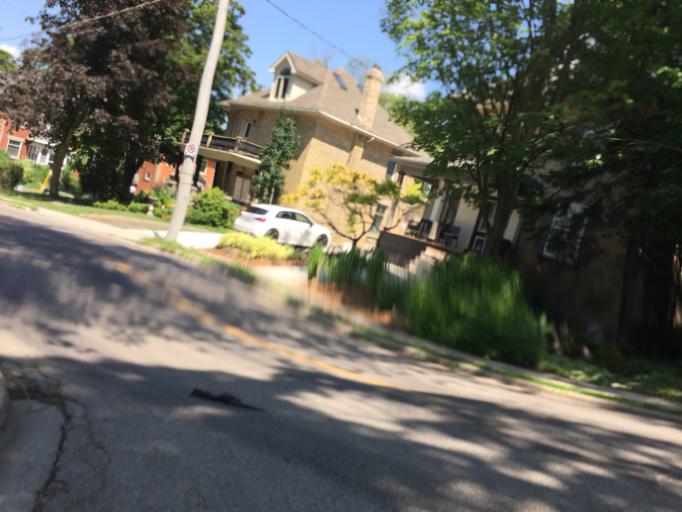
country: CA
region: Ontario
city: Stratford
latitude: 43.3737
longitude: -80.9734
